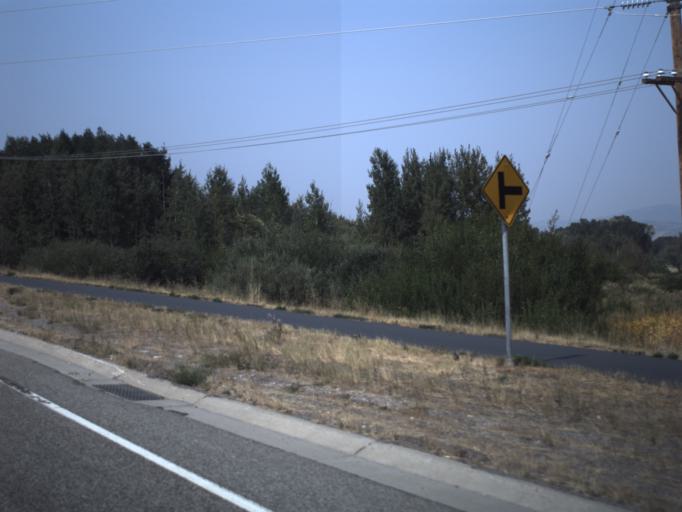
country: US
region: Utah
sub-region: Summit County
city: Snyderville
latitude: 40.6828
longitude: -111.5354
